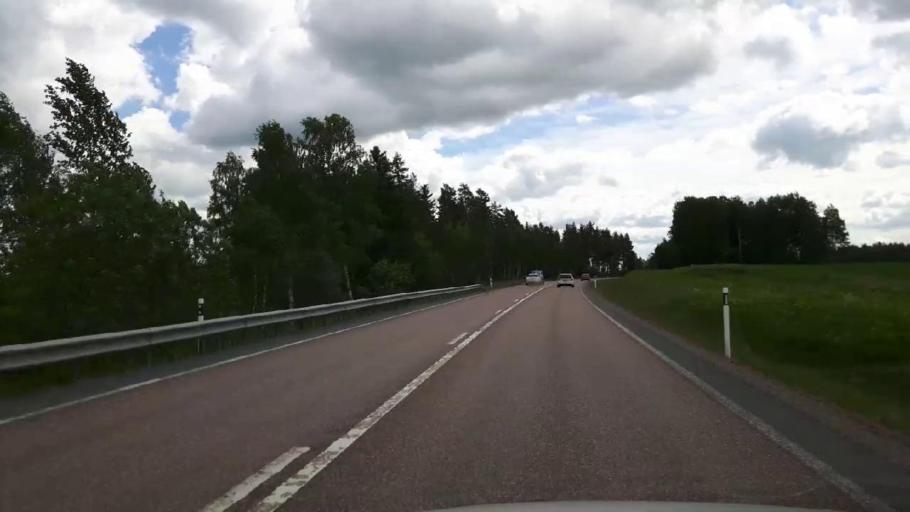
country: SE
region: Dalarna
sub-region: Saters Kommun
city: Saeter
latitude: 60.4717
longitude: 15.7943
